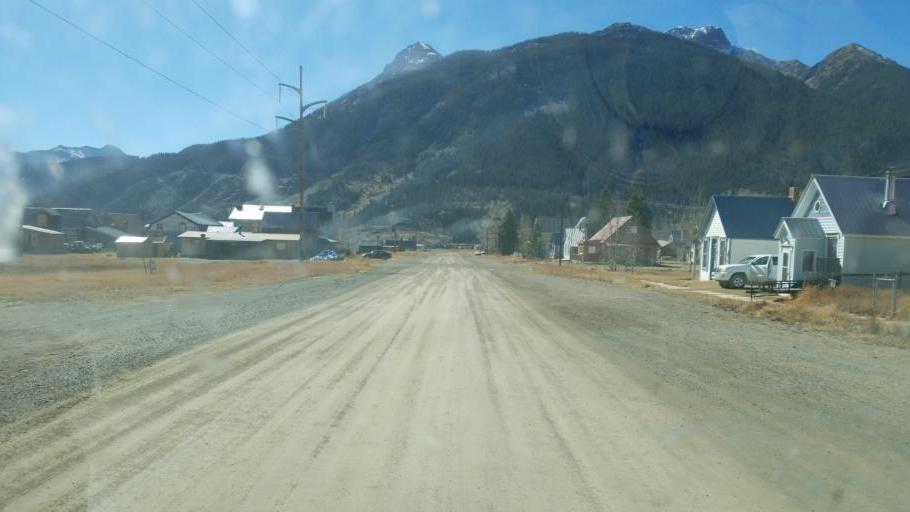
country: US
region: Colorado
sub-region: San Juan County
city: Silverton
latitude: 37.8090
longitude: -107.6638
